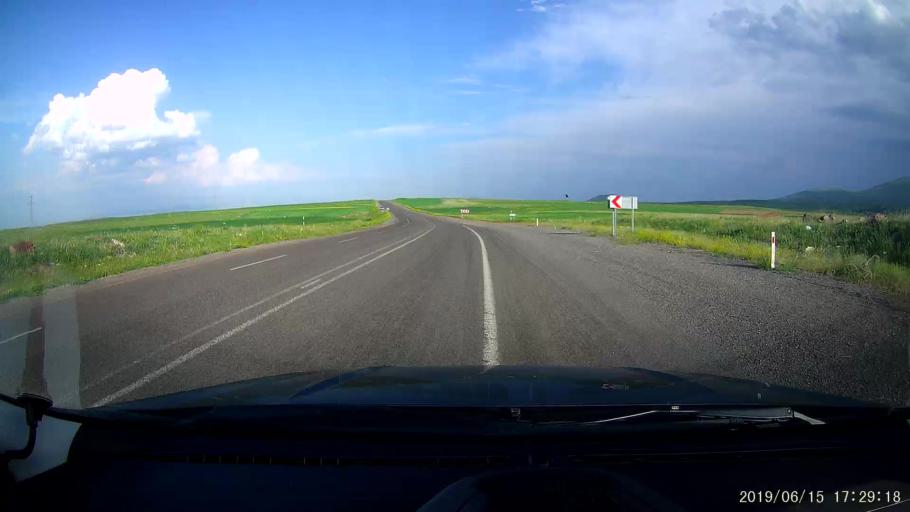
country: TR
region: Kars
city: Basgedikler
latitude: 40.5904
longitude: 43.4508
